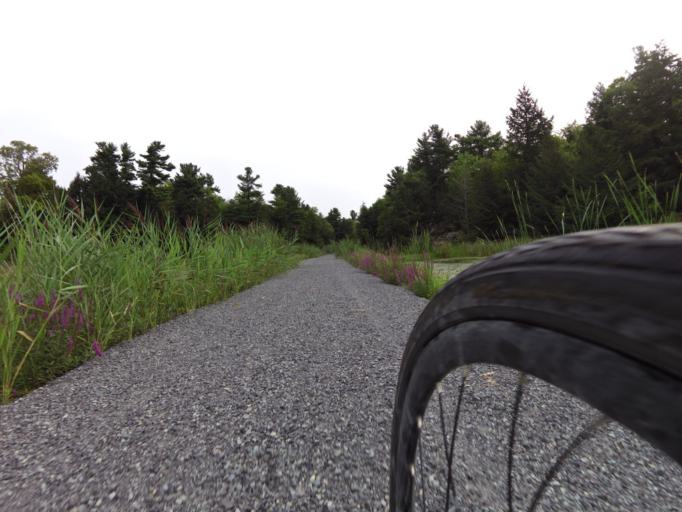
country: CA
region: Ontario
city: Gananoque
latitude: 44.6036
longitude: -76.2891
